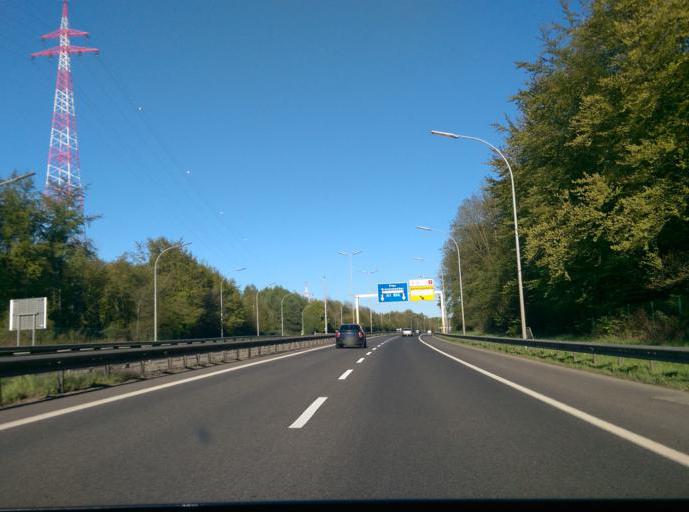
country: LU
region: Luxembourg
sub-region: Canton de Luxembourg
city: Sandweiler
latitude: 49.6426
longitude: 6.2087
